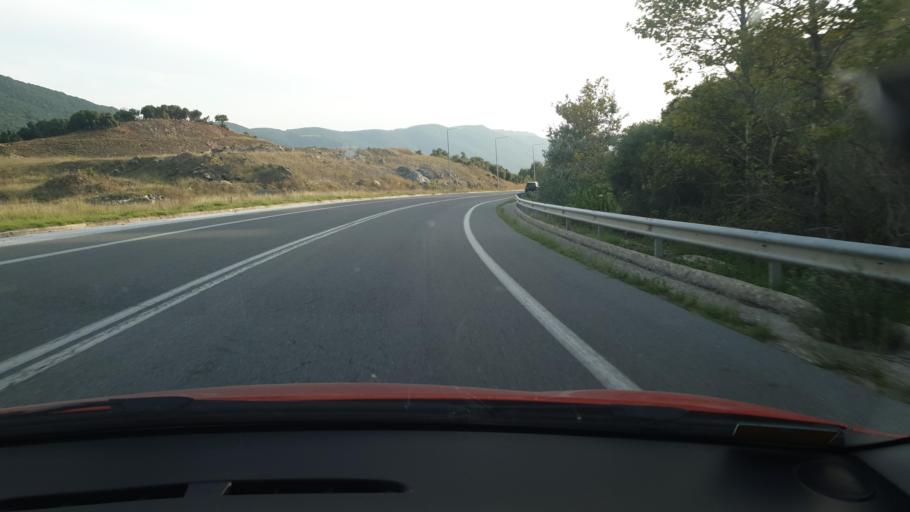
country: GR
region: Central Macedonia
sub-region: Nomos Chalkidikis
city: Galatista
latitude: 40.4585
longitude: 23.3217
